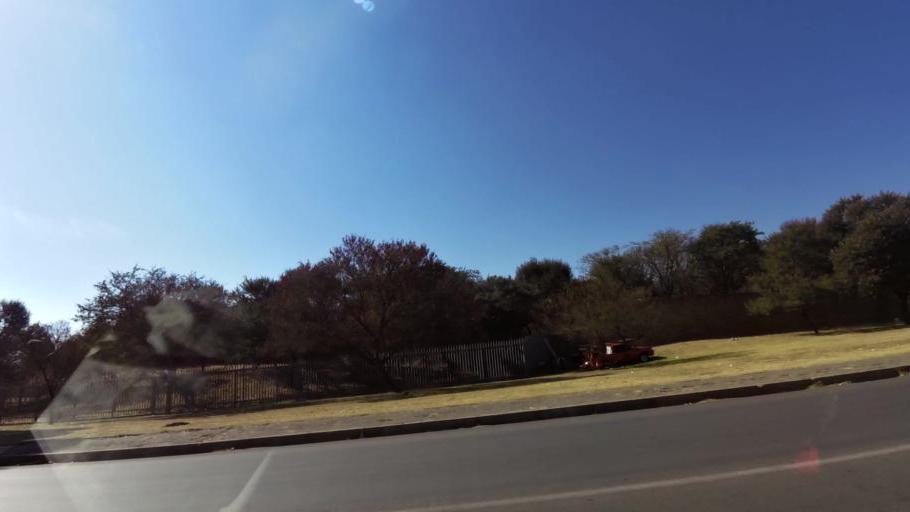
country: ZA
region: Gauteng
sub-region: City of Johannesburg Metropolitan Municipality
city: Johannesburg
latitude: -26.2334
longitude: 28.0032
